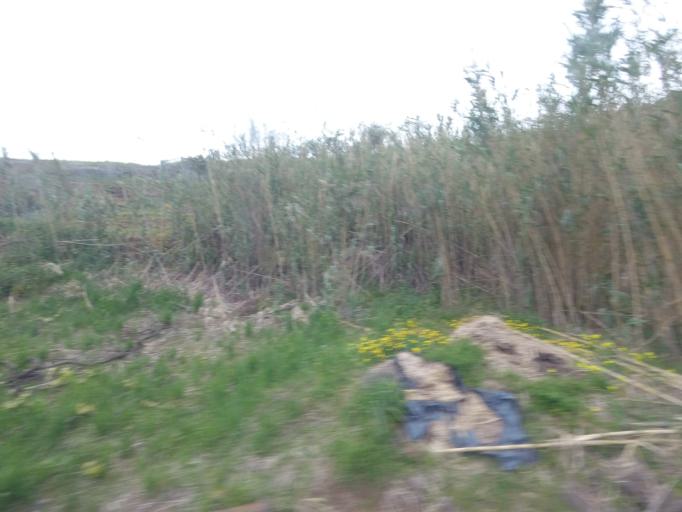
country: PT
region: Madeira
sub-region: Santana
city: Santana
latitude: 32.7648
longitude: -16.8148
